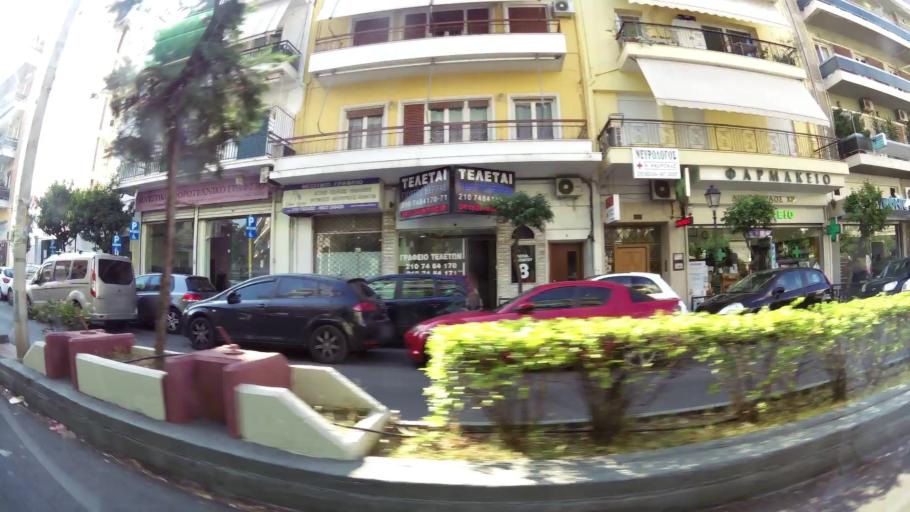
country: GR
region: Attica
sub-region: Nomarchia Athinas
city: Kaisariani
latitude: 37.9800
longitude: 23.7620
